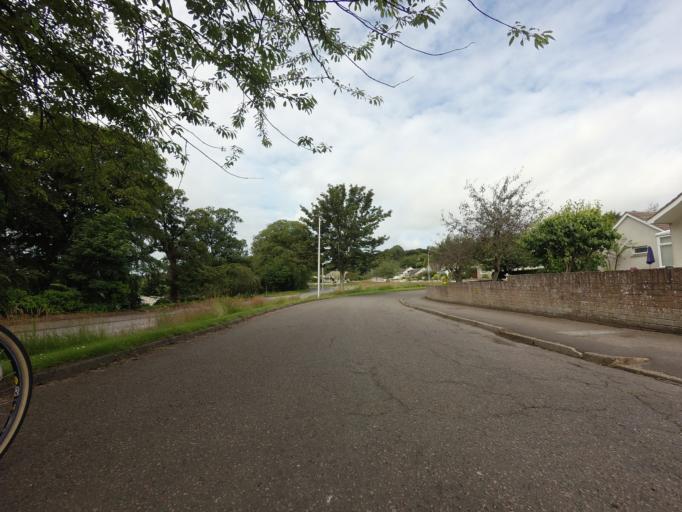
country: GB
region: Scotland
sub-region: Moray
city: Elgin
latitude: 57.6524
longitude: -3.3354
